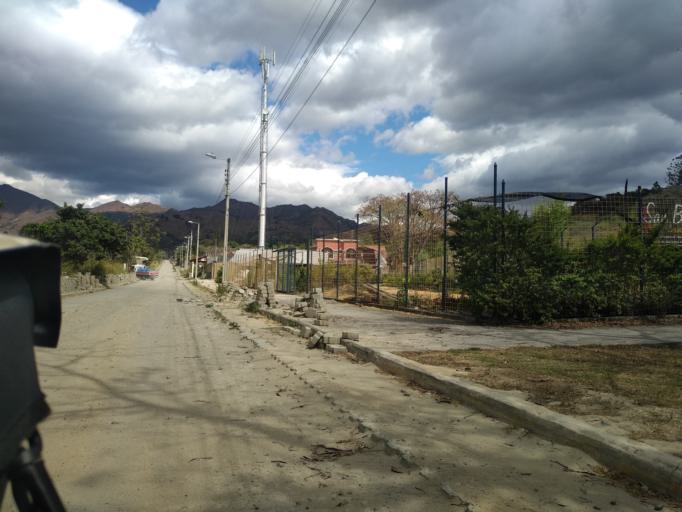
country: EC
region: Loja
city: Loja
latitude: -4.2526
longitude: -79.2245
